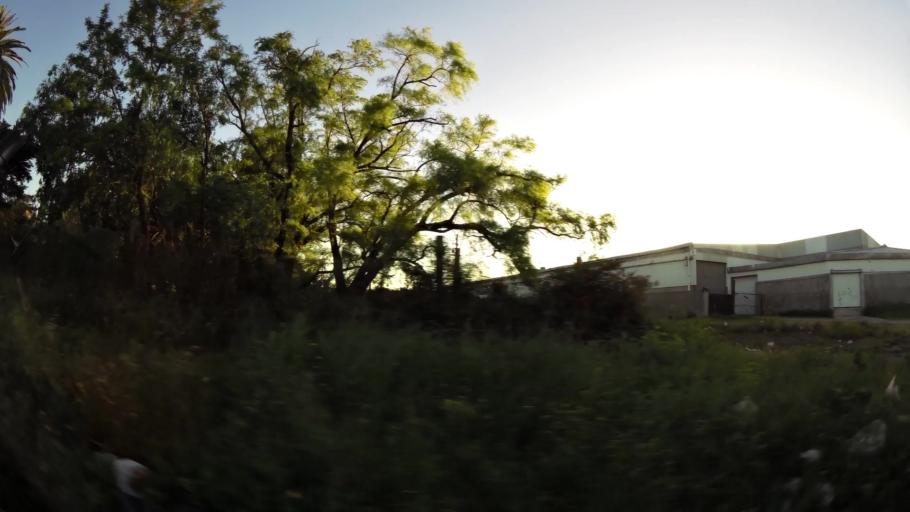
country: UY
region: Montevideo
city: Montevideo
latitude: -34.8457
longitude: -56.1593
